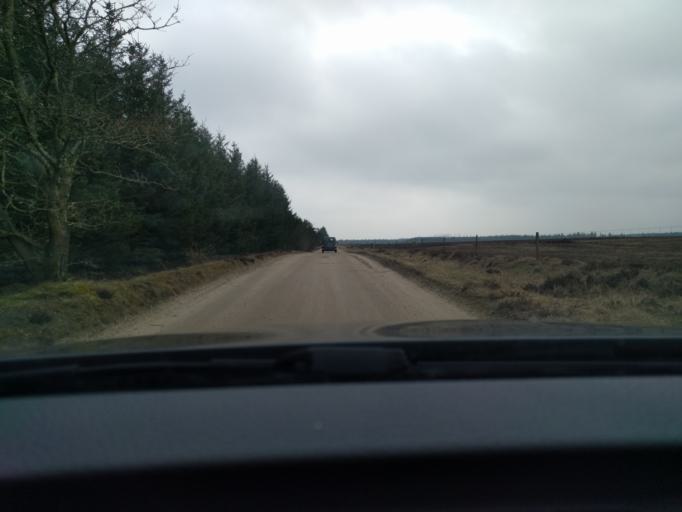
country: DK
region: Central Jutland
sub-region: Skive Kommune
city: Skive
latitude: 56.5053
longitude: 8.9420
